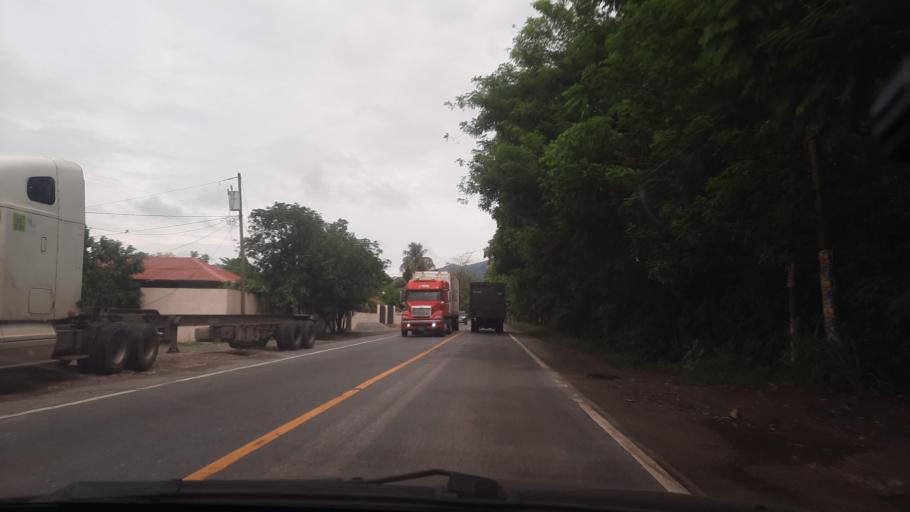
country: GT
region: Izabal
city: Morales
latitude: 15.4642
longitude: -88.9142
